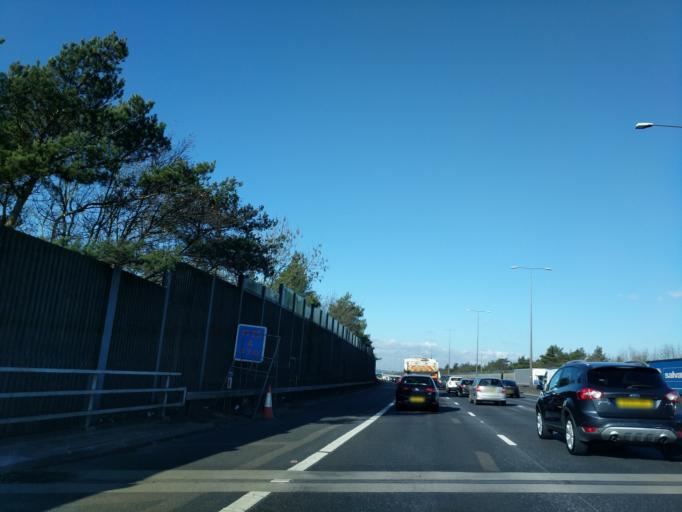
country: GB
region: England
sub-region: Surrey
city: Byfleet
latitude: 51.3497
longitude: -0.4871
